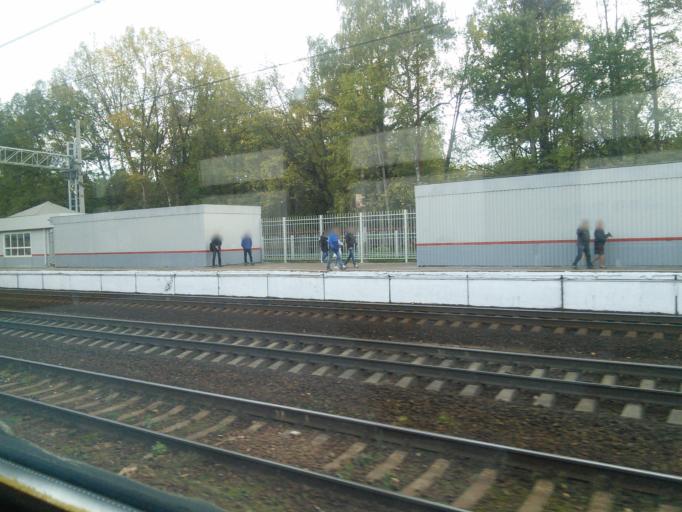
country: RU
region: Moskovskaya
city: Levoberezhnaya
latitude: 55.8873
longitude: 37.4682
